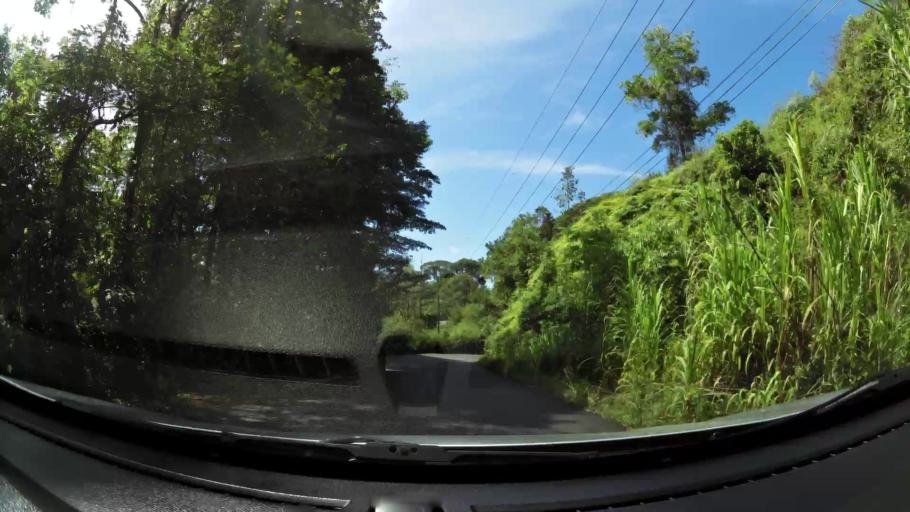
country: CR
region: San Jose
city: San Isidro
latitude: 9.2792
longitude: -83.8222
